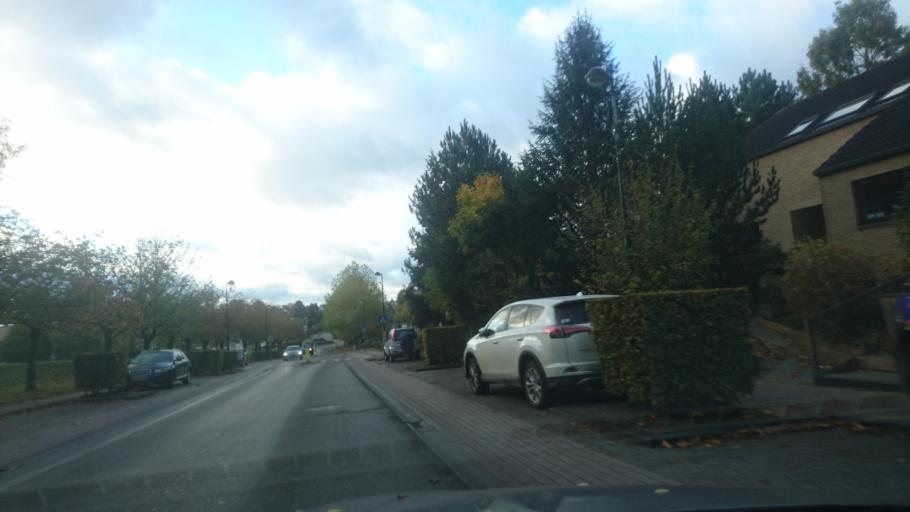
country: BE
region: Wallonia
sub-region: Province du Brabant Wallon
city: Waterloo
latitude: 50.7131
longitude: 4.3971
